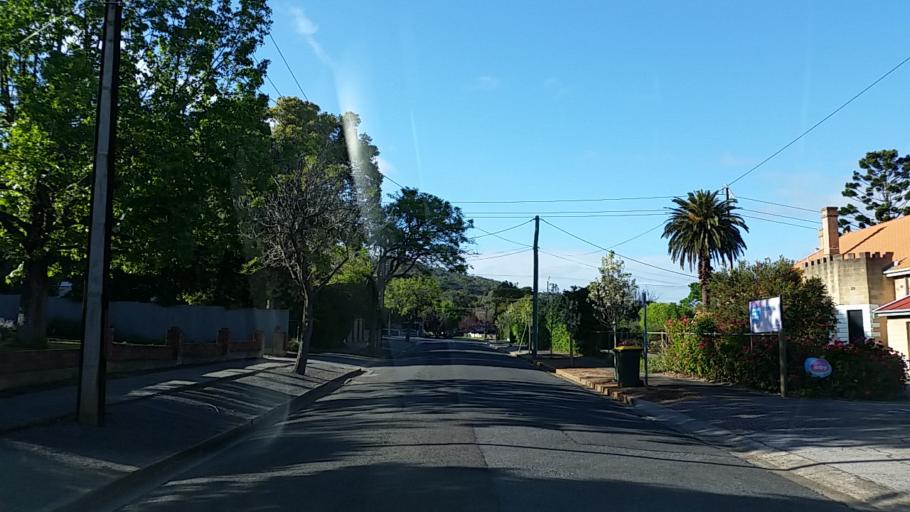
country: AU
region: South Australia
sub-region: Mitcham
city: Clapham
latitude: -34.9893
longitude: 138.6037
